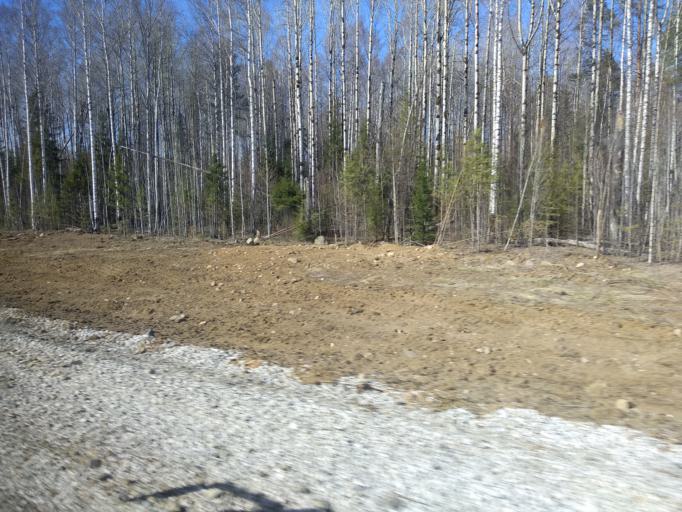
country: RU
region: Sverdlovsk
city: Krasnotur'insk
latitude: 59.6686
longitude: 60.1847
